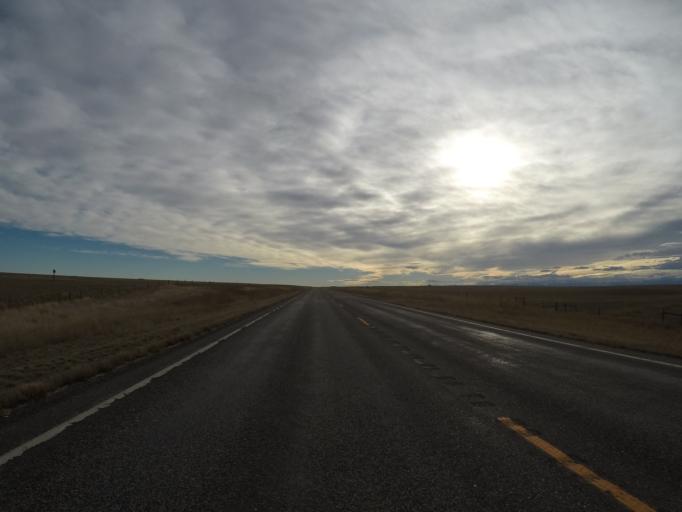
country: US
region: Montana
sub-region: Yellowstone County
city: Laurel
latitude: 45.8483
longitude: -108.8812
